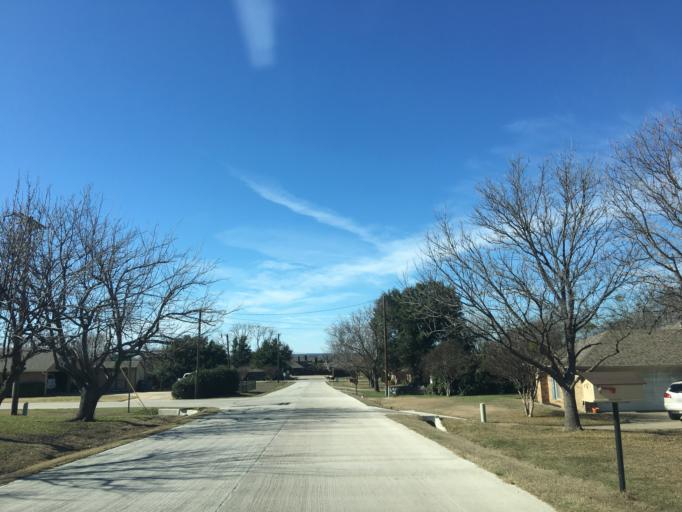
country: US
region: Texas
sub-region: Collin County
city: Prosper
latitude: 33.2403
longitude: -96.7967
